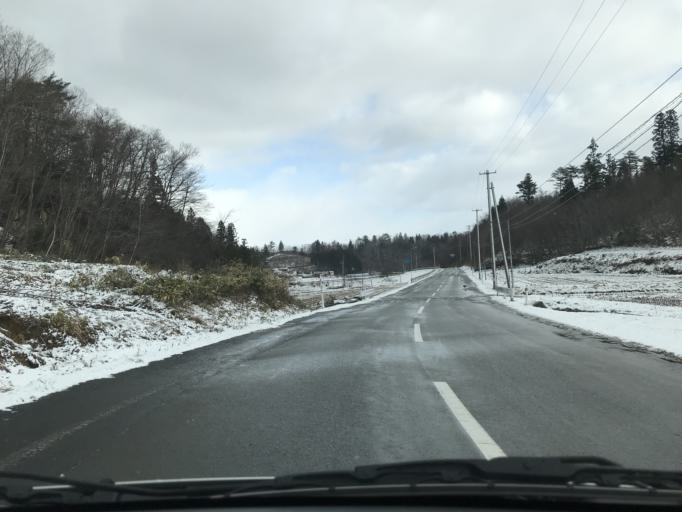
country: JP
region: Iwate
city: Ichinoseki
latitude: 38.9934
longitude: 140.9595
